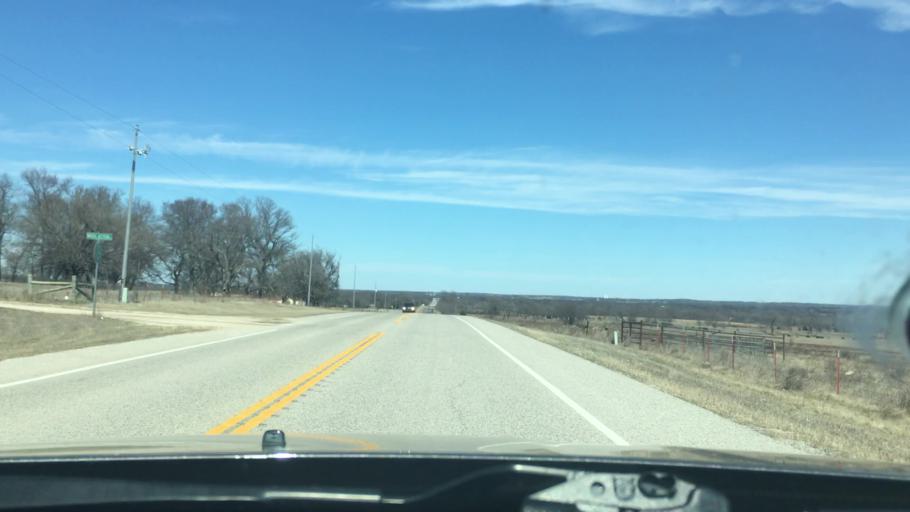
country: US
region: Oklahoma
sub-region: Murray County
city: Sulphur
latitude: 34.3467
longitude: -96.9508
